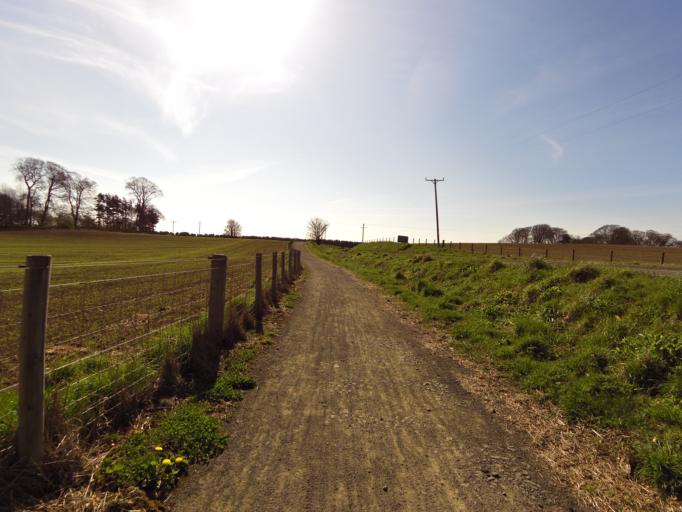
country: GB
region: Scotland
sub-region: Angus
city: Montrose
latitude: 56.7467
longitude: -2.4539
